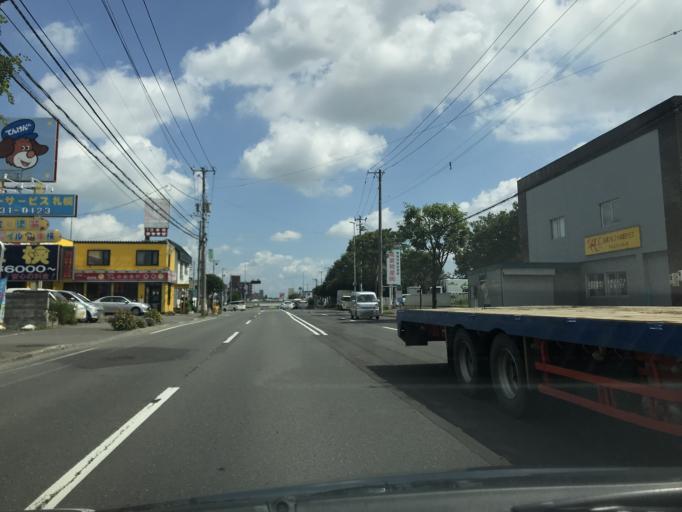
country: JP
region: Hokkaido
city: Sapporo
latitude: 43.0643
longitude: 141.3917
